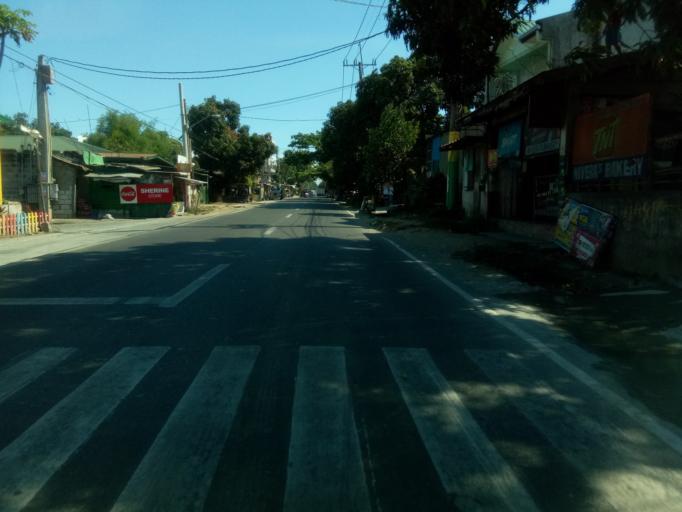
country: PH
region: Calabarzon
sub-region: Province of Cavite
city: Bulihan
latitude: 14.2986
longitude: 120.9914
